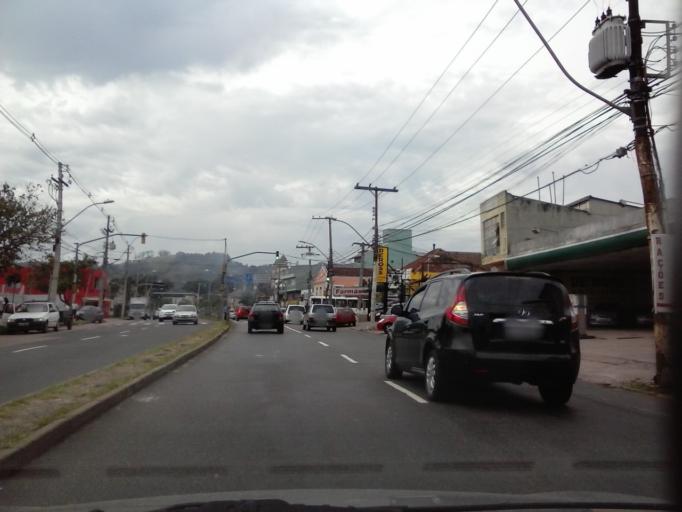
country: BR
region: Rio Grande do Sul
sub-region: Porto Alegre
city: Porto Alegre
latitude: -30.0724
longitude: -51.2036
